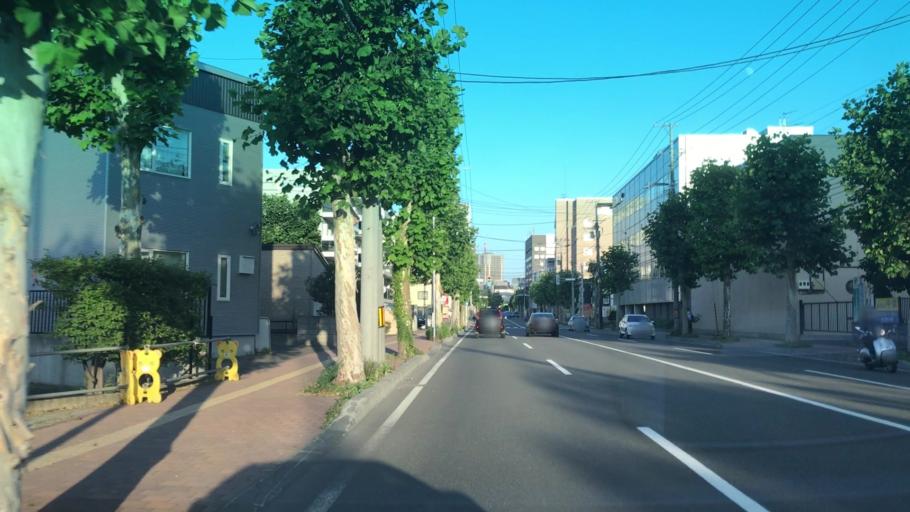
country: JP
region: Hokkaido
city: Sapporo
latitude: 43.0736
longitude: 141.3272
